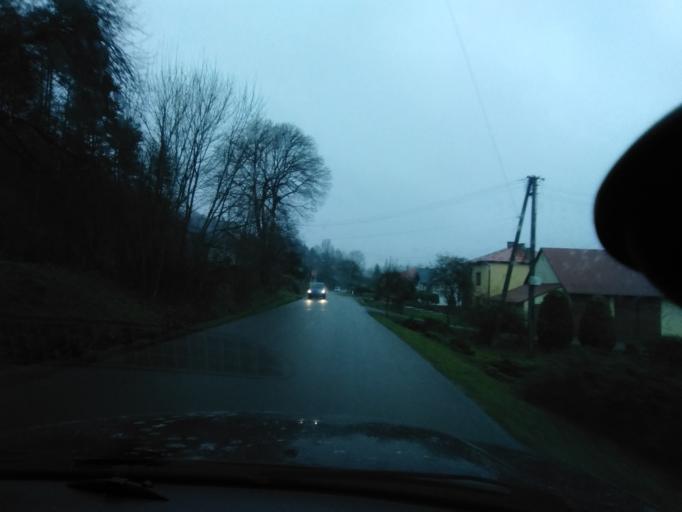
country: PL
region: Subcarpathian Voivodeship
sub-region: Powiat brzozowski
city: Jablonka
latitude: 49.7424
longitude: 22.1309
